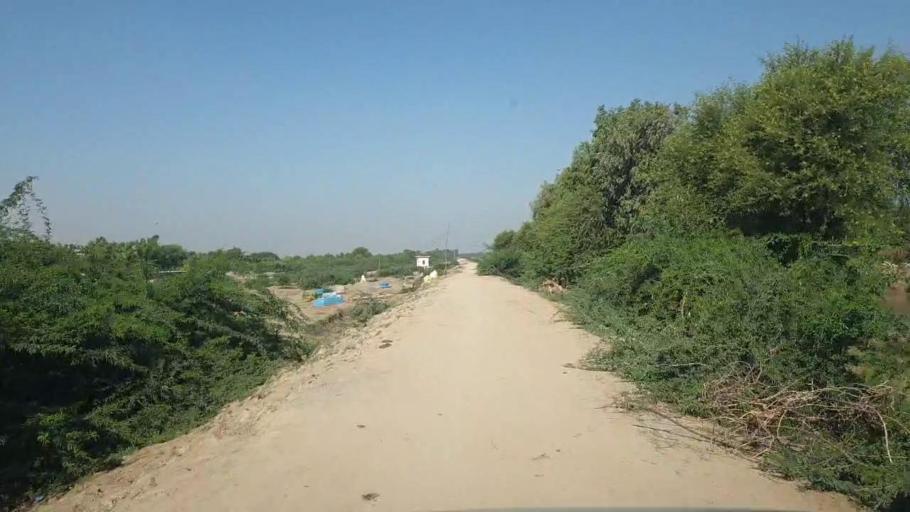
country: PK
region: Sindh
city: Talhar
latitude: 24.7920
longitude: 68.8033
